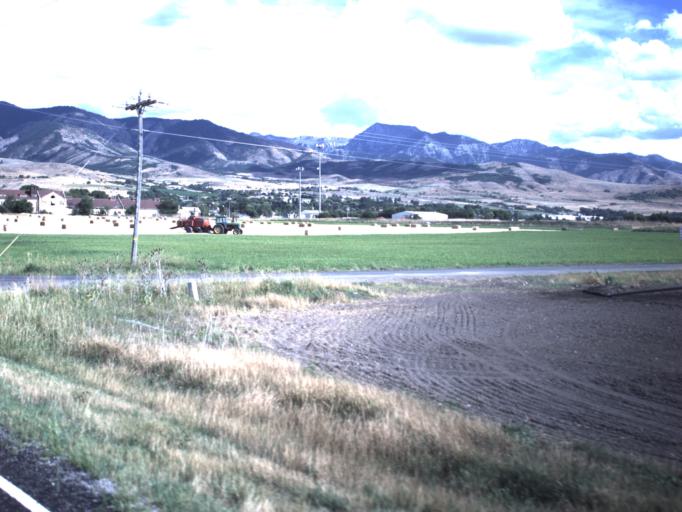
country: US
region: Utah
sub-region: Cache County
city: Richmond
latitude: 41.9229
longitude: -111.8296
